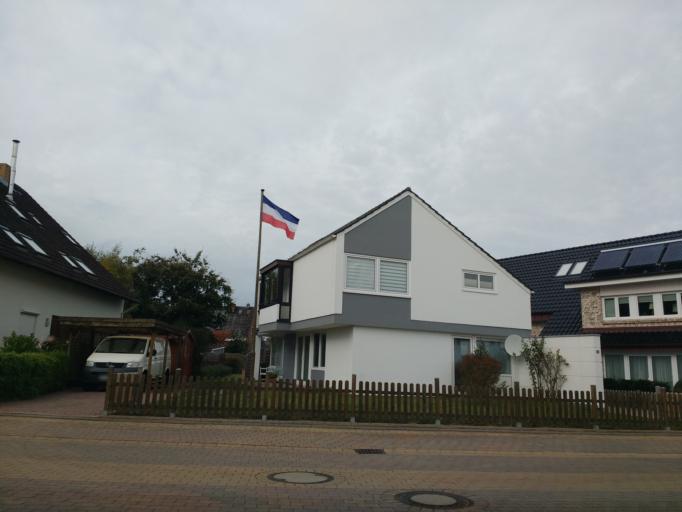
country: DE
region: Schleswig-Holstein
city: Gromitz
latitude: 54.1517
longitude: 10.9740
